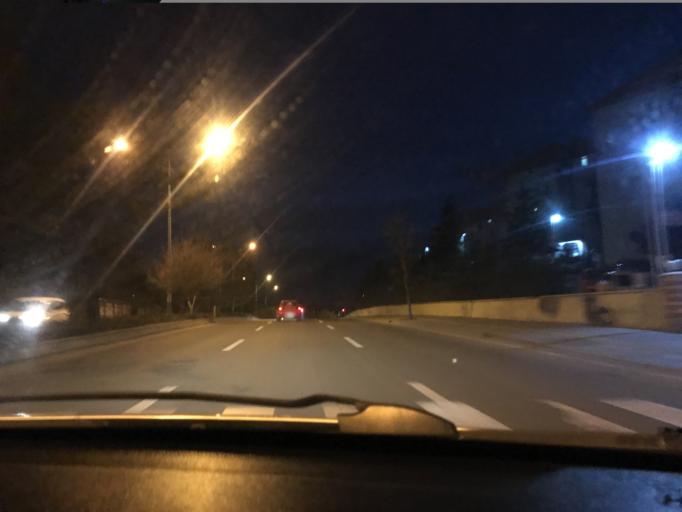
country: TR
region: Ankara
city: Batikent
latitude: 39.9609
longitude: 32.7313
